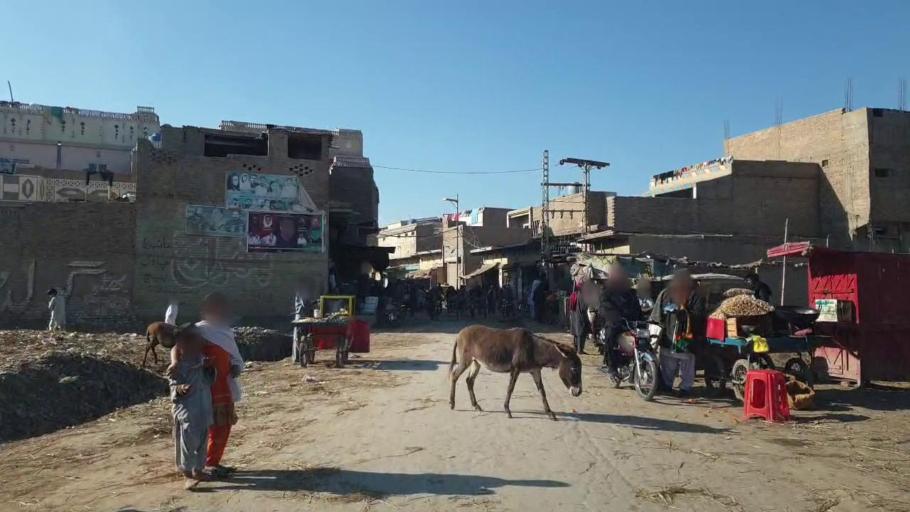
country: PK
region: Sindh
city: New Badah
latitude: 27.3279
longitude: 68.0276
